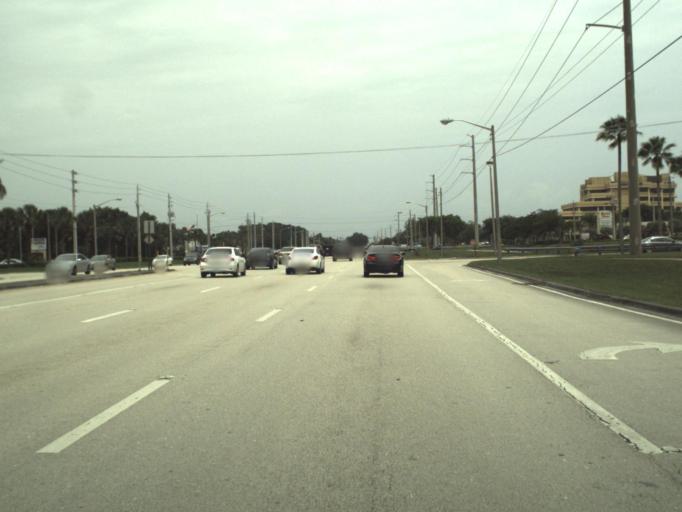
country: US
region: Florida
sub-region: Palm Beach County
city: Boca Del Mar
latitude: 26.3502
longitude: -80.1591
